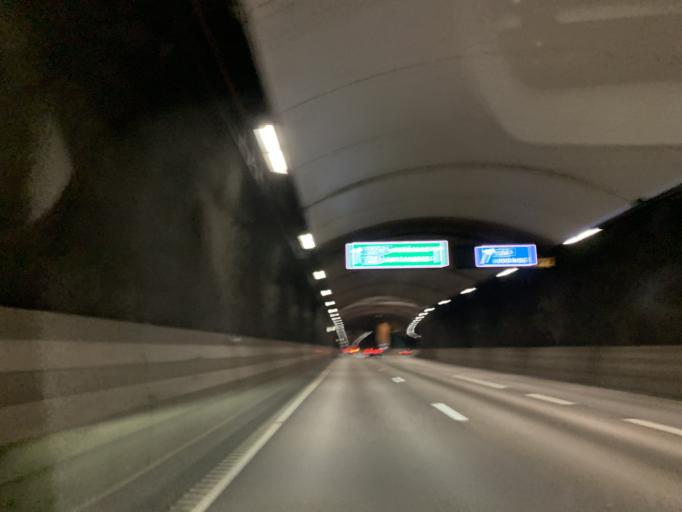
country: SE
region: Stockholm
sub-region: Stockholms Kommun
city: Arsta
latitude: 59.2962
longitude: 18.0484
